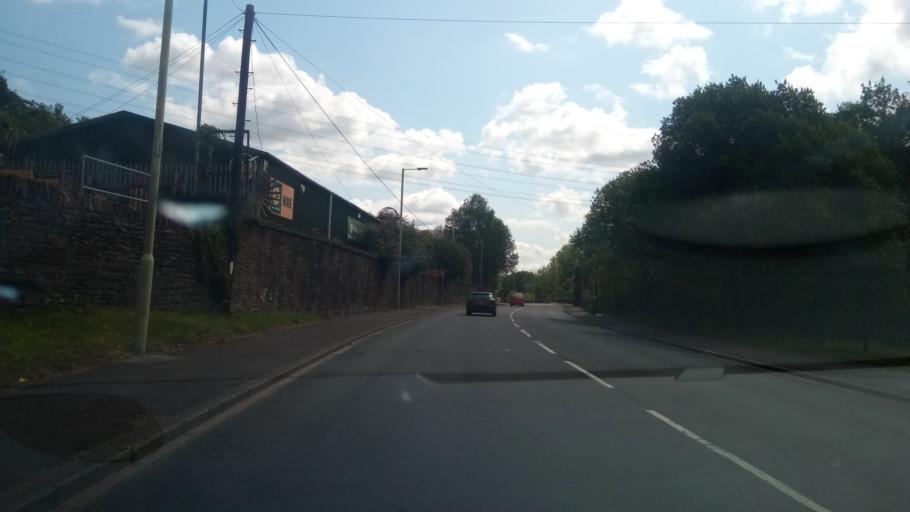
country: GB
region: Wales
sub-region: Rhondda Cynon Taf
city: Pontypridd
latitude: 51.6098
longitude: -3.3690
